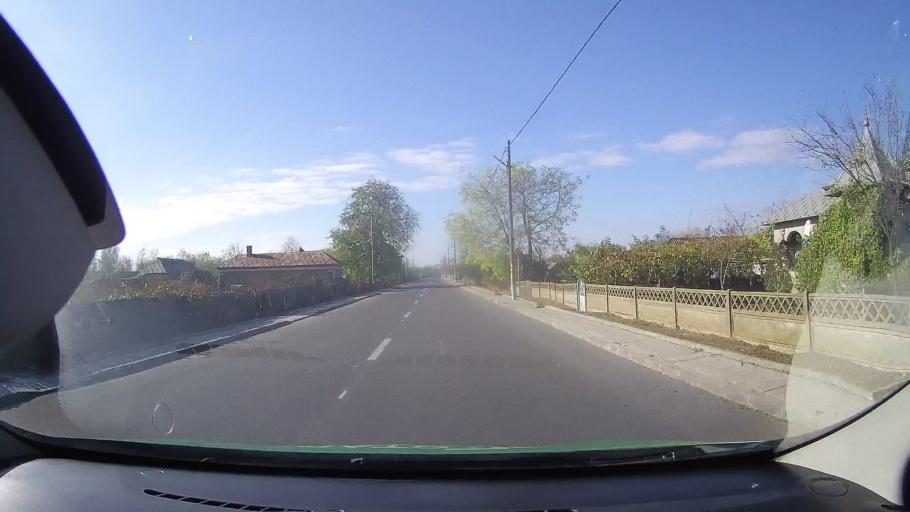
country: RO
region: Tulcea
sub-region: Comuna Murighiol
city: Murighiol
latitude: 45.0225
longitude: 29.1289
